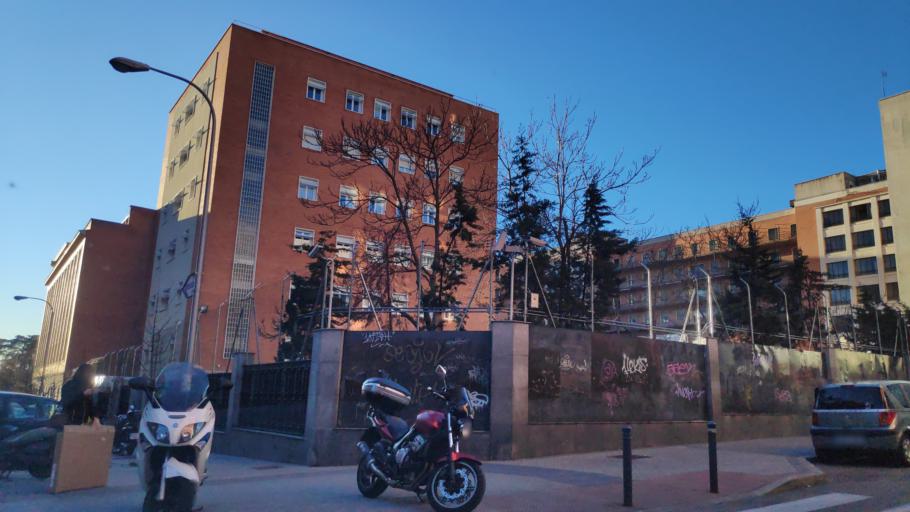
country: ES
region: Madrid
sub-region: Provincia de Madrid
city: Chamberi
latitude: 40.4366
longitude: -3.7166
